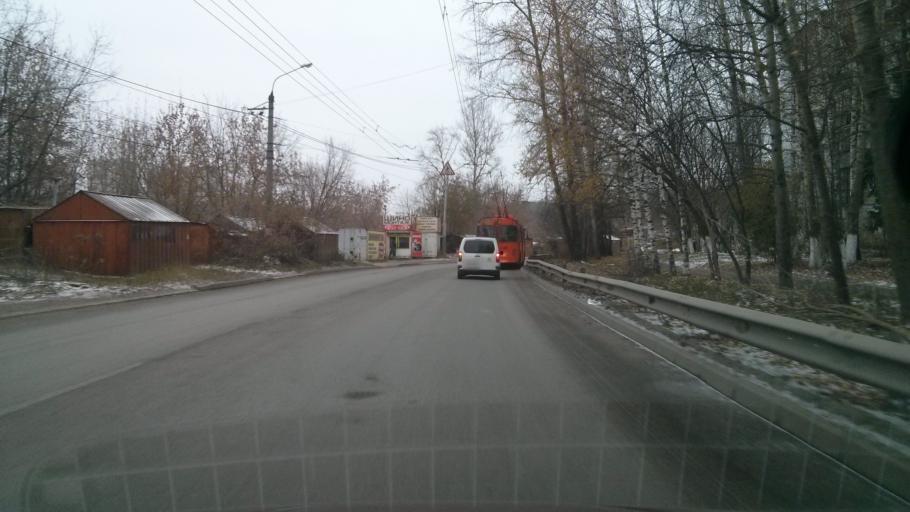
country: RU
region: Nizjnij Novgorod
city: Afonino
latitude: 56.2930
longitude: 44.0542
